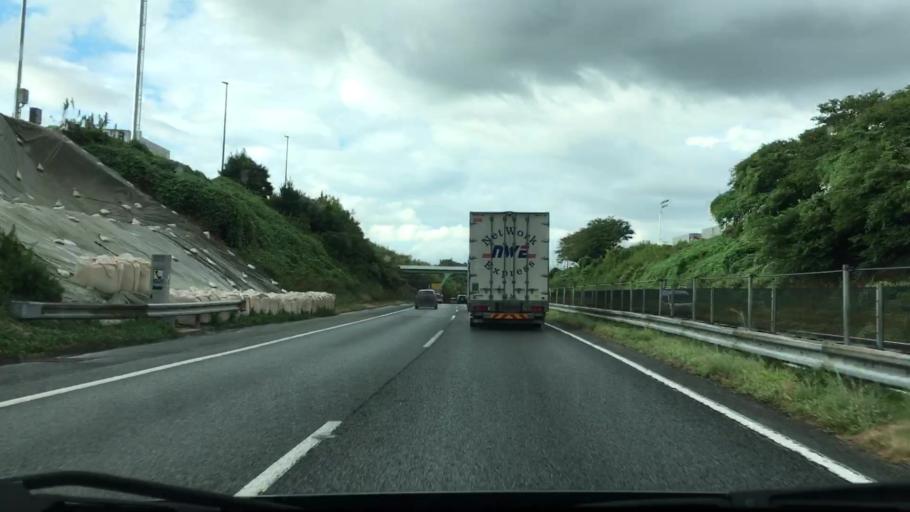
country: JP
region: Fukuoka
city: Koga
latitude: 33.7374
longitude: 130.5182
